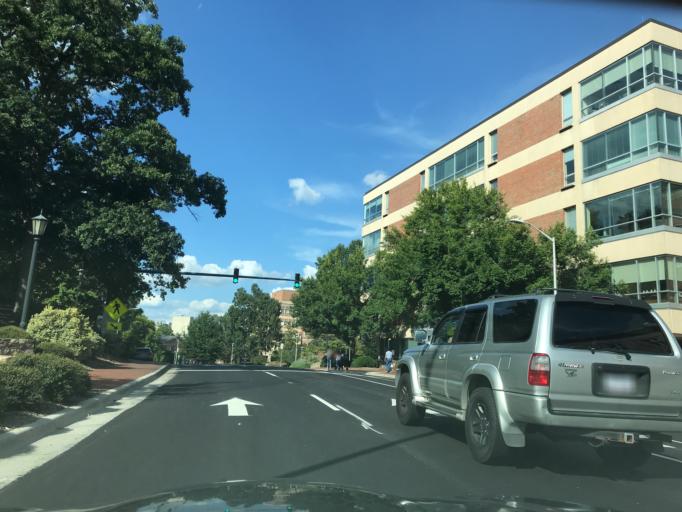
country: US
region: North Carolina
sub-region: Orange County
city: Chapel Hill
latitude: 35.9055
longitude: -79.0535
